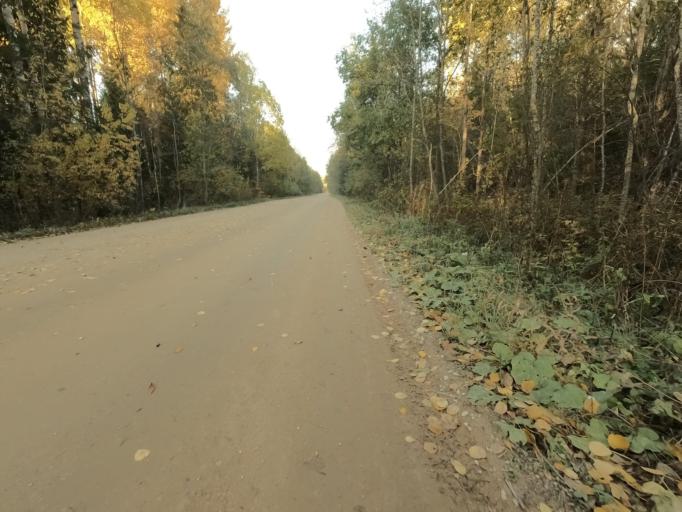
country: RU
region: Leningrad
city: Lyuban'
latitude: 58.9876
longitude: 31.1007
